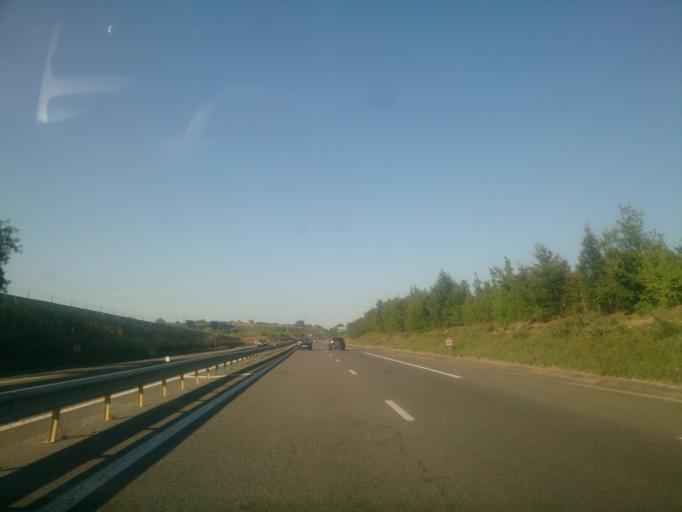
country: FR
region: Midi-Pyrenees
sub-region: Departement du Tarn-et-Garonne
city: Caussade
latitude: 44.1576
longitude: 1.5172
